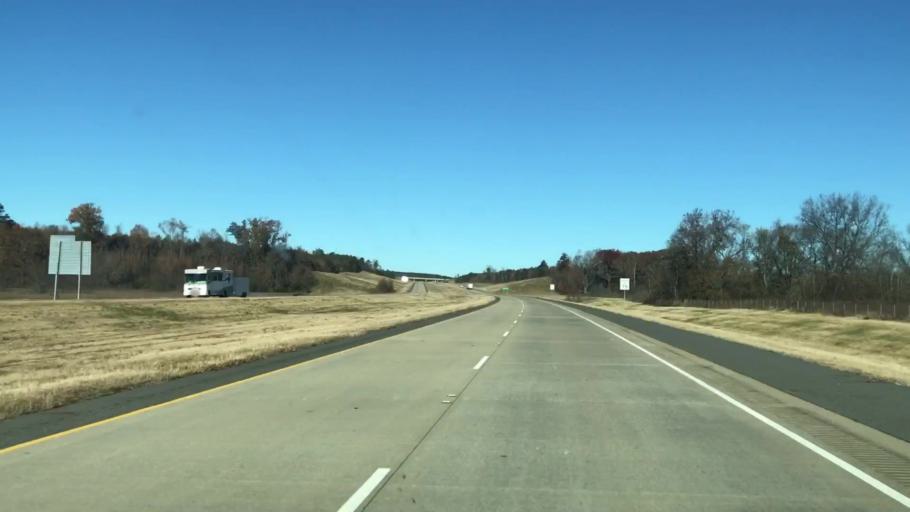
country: US
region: Louisiana
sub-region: Caddo Parish
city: Vivian
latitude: 32.9086
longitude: -93.8685
